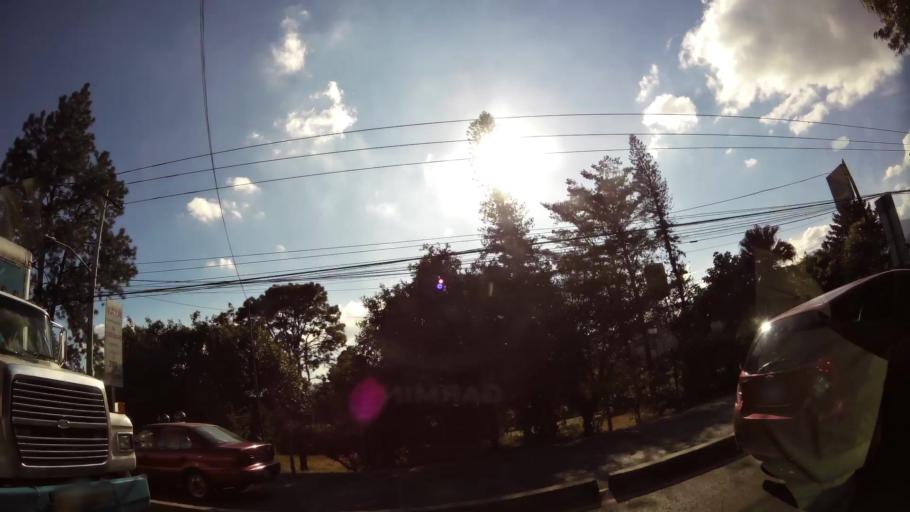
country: GT
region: Guatemala
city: Villa Nueva
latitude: 14.5143
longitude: -90.5751
